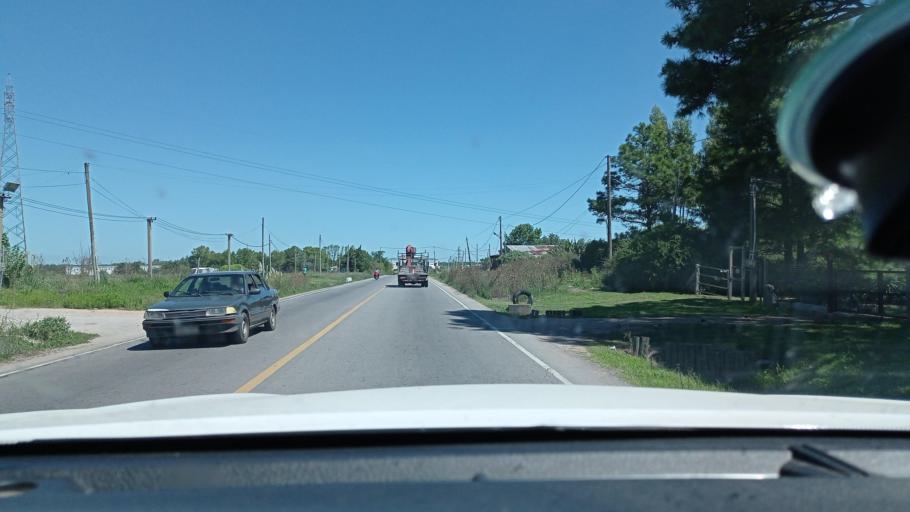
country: UY
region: Canelones
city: La Paz
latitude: -34.7801
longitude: -56.1674
